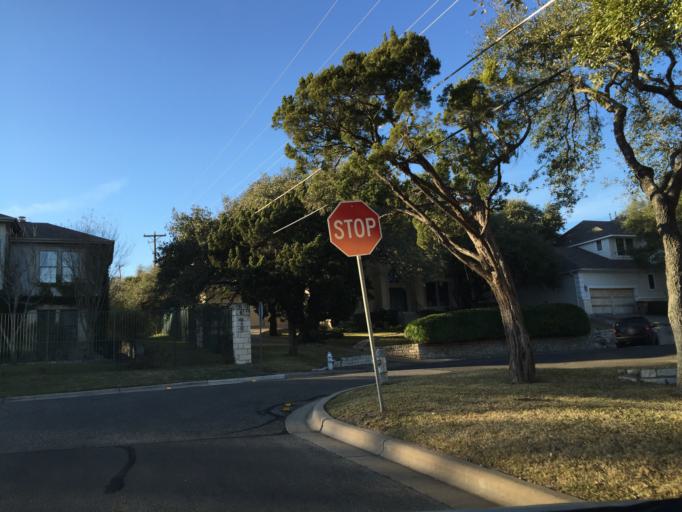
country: US
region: Texas
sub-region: Travis County
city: Rollingwood
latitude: 30.2727
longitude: -97.8201
